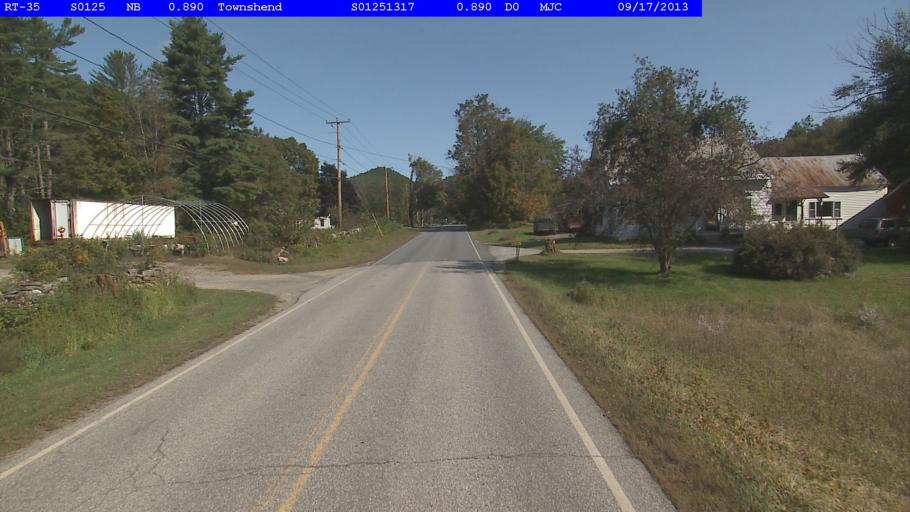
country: US
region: Vermont
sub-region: Windham County
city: Newfane
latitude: 43.0583
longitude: -72.6626
